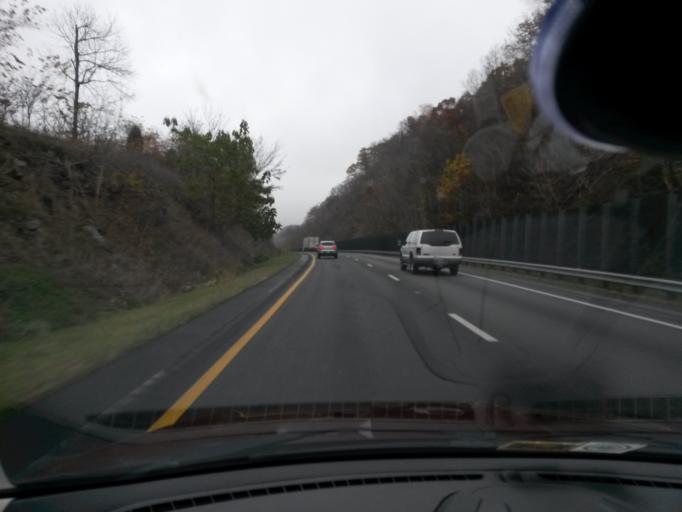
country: US
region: Virginia
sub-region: Montgomery County
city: Shawsville
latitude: 37.1855
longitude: -80.2845
